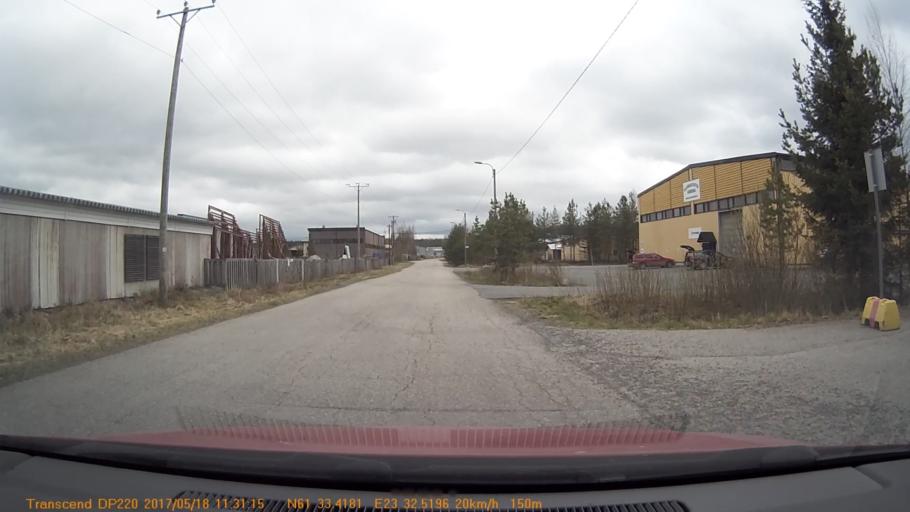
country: FI
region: Pirkanmaa
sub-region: Tampere
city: Yloejaervi
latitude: 61.5569
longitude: 23.5420
